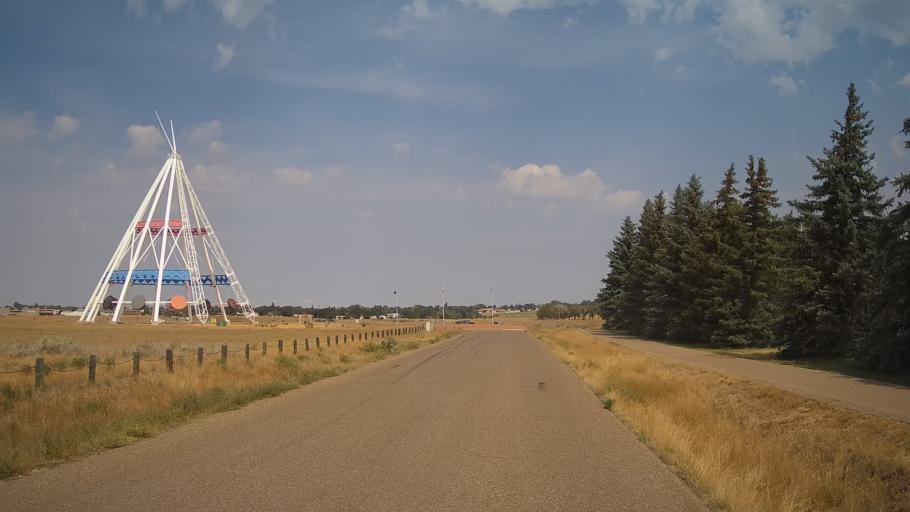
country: CA
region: Alberta
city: Medicine Hat
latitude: 50.0136
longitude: -110.6905
